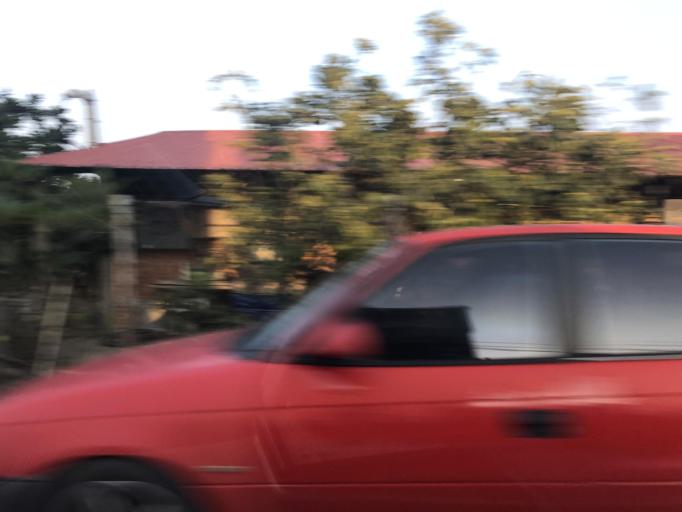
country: TW
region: Taiwan
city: Xinying
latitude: 23.1881
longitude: 120.2534
